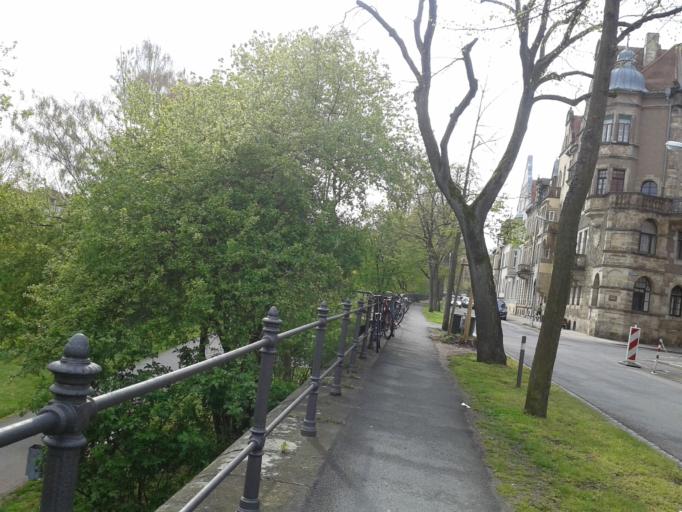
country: DE
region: Bavaria
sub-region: Upper Franconia
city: Bamberg
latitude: 49.8936
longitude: 10.8955
